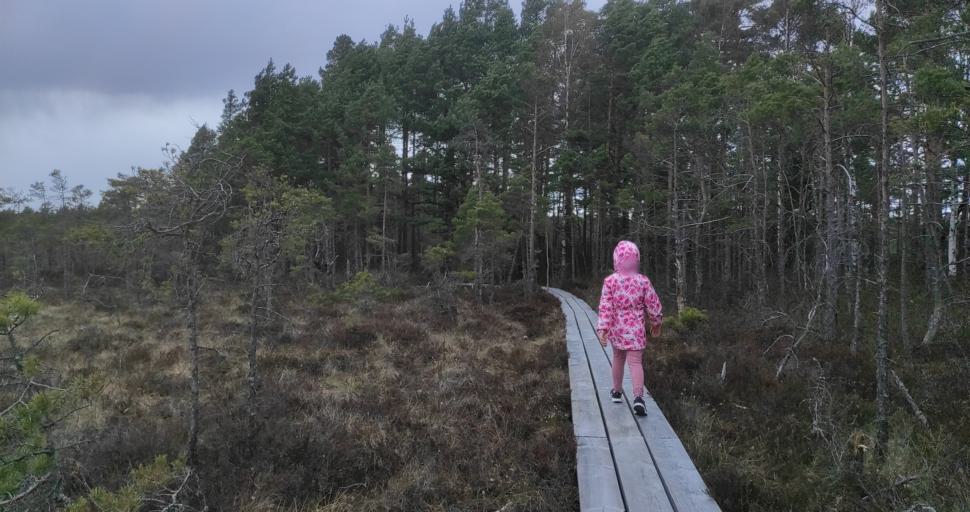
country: LV
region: Dundaga
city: Dundaga
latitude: 57.3443
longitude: 22.1554
